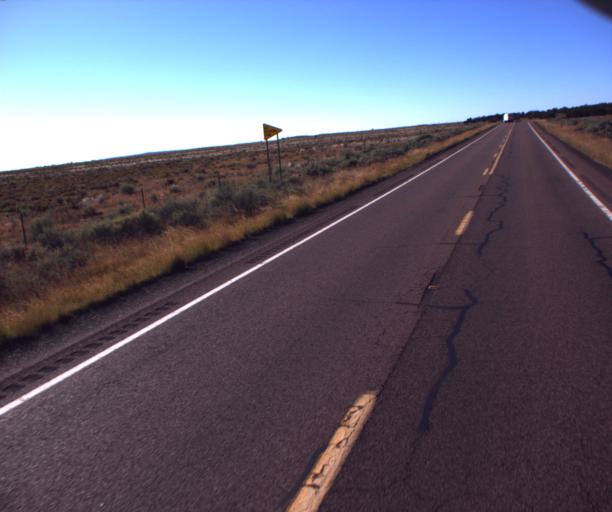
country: US
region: Arizona
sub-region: Navajo County
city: Heber-Overgaard
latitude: 34.5625
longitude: -110.4140
